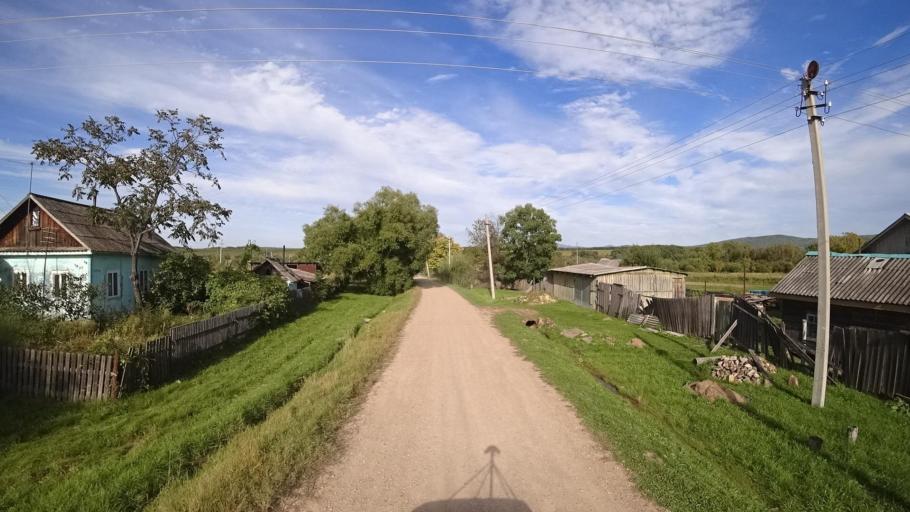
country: RU
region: Primorskiy
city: Dostoyevka
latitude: 44.3016
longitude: 133.4587
